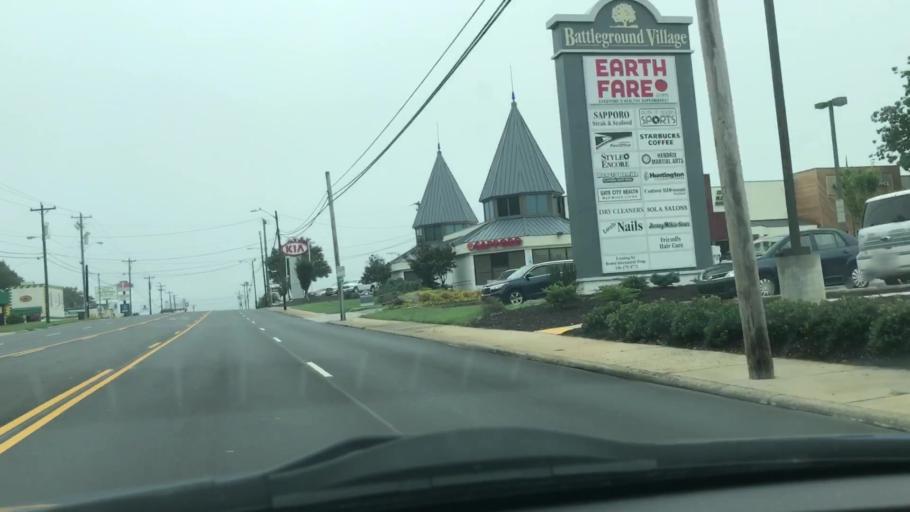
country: US
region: North Carolina
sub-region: Guilford County
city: Greensboro
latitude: 36.1149
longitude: -79.8352
